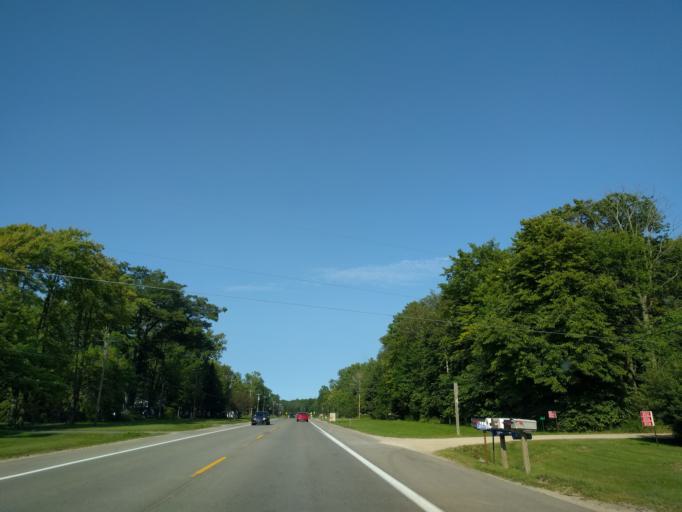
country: US
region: Michigan
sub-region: Menominee County
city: Menominee
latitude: 45.1530
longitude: -87.5975
